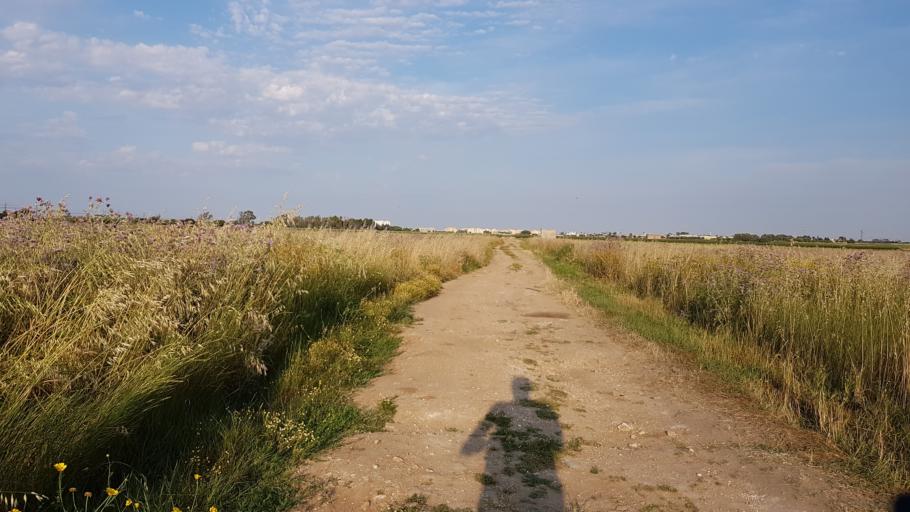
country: IT
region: Apulia
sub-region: Provincia di Brindisi
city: Brindisi
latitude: 40.6248
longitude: 17.8854
